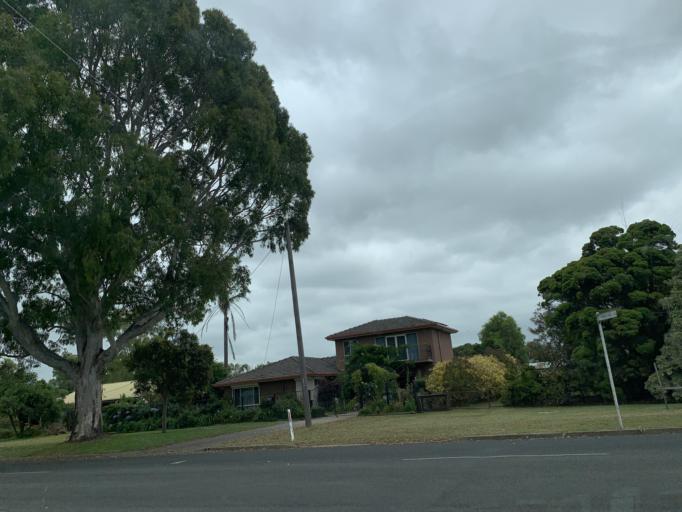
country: AU
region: Victoria
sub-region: Wellington
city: Heyfield
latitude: -37.9789
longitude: 146.7945
